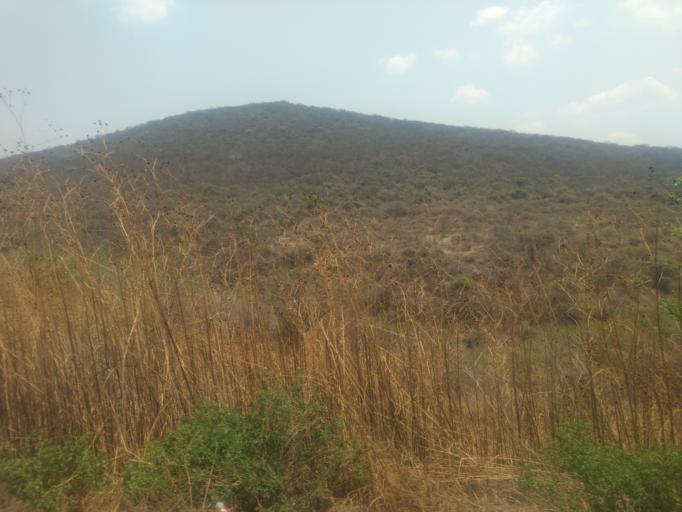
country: MX
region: Morelos
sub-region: Mazatepec
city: Cuauchichinola
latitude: 18.6521
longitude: -99.4026
